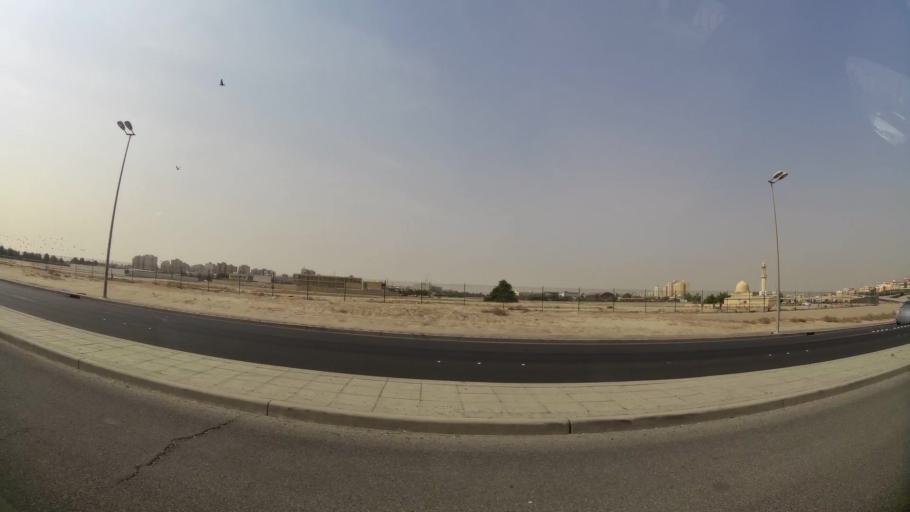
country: KW
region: Al Farwaniyah
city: Al Farwaniyah
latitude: 29.2629
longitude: 47.9526
